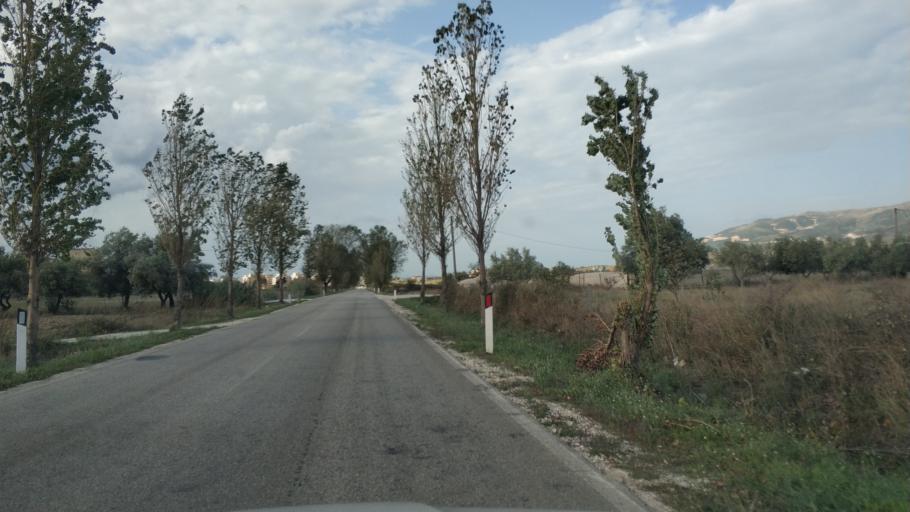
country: AL
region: Vlore
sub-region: Rrethi i Vlores
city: Orikum
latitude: 40.3191
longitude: 19.4829
